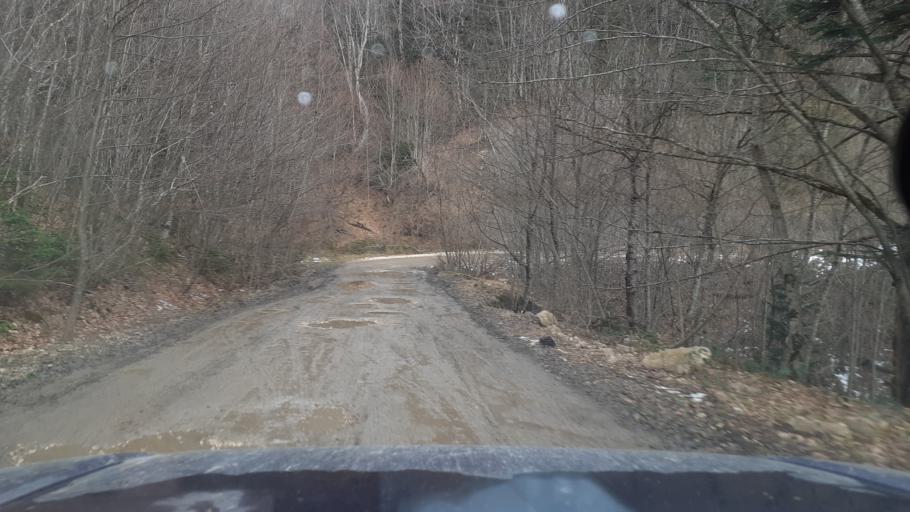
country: RU
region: Krasnodarskiy
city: Neftegorsk
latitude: 44.0794
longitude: 39.7450
